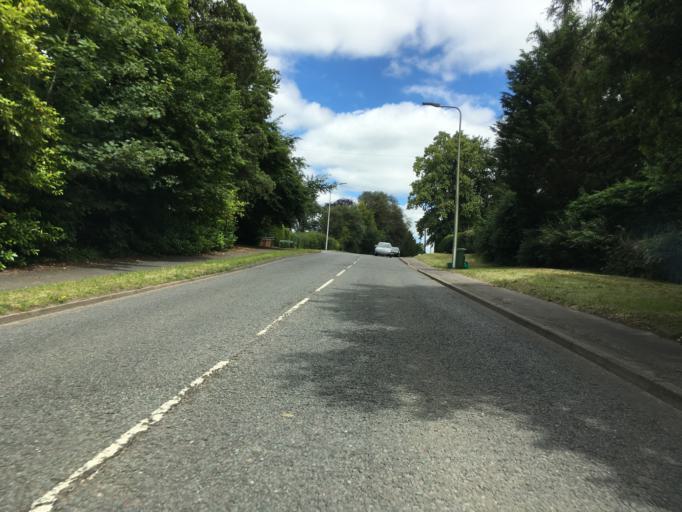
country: GB
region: England
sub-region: West Berkshire
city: Newbury
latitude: 51.3717
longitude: -1.3469
